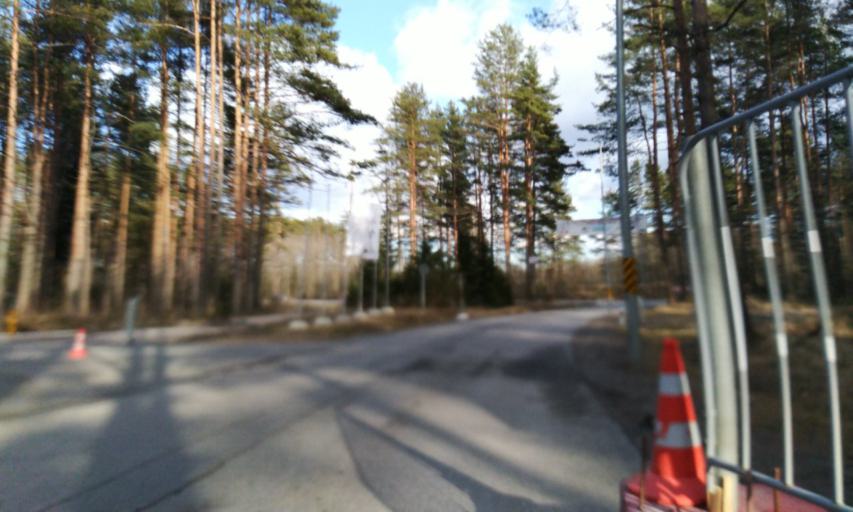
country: RU
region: Leningrad
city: Toksovo
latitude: 60.1273
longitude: 30.4624
